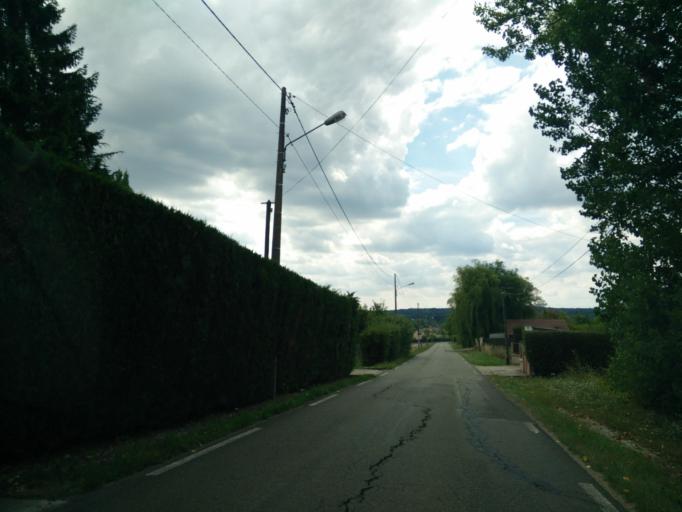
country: FR
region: Ile-de-France
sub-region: Departement des Yvelines
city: Garancieres
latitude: 48.8290
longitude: 1.7602
